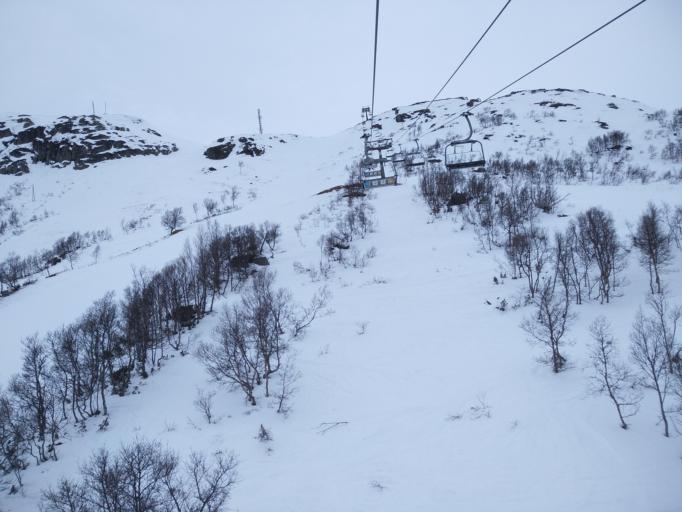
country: NO
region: Aust-Agder
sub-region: Bykle
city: Hovden
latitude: 59.5759
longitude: 7.3383
